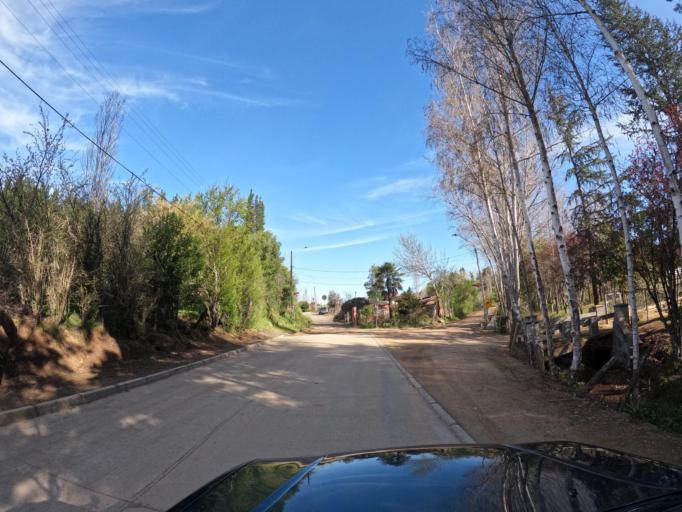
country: CL
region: Biobio
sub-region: Provincia de Biobio
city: La Laja
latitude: -37.1367
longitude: -72.7259
